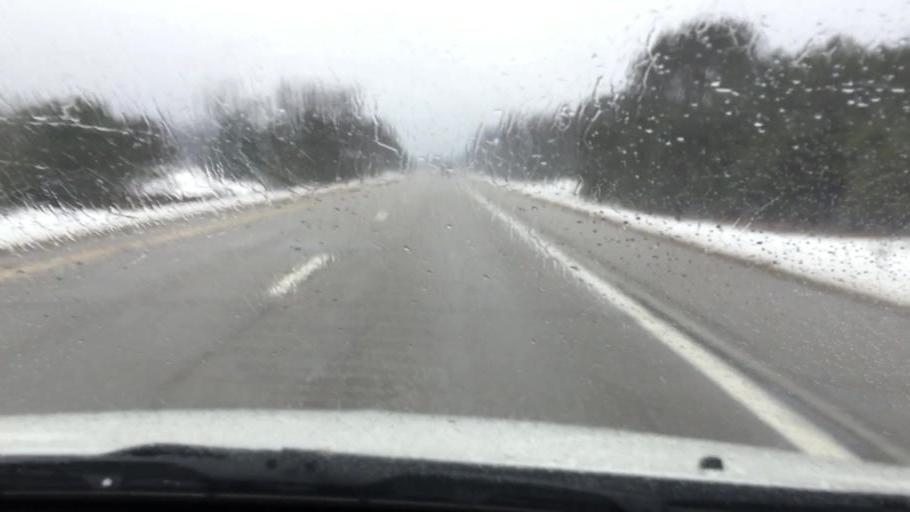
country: US
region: Michigan
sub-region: Wexford County
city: Cadillac
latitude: 44.1523
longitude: -85.4587
